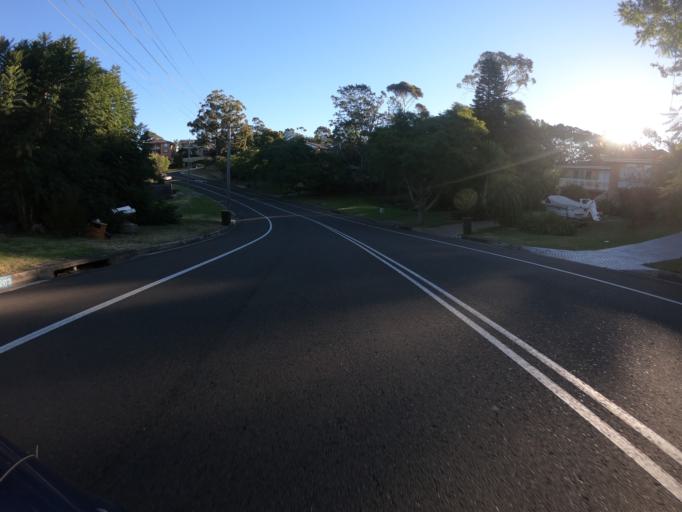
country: AU
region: New South Wales
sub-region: Wollongong
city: Cordeaux Heights
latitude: -34.4330
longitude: 150.8470
